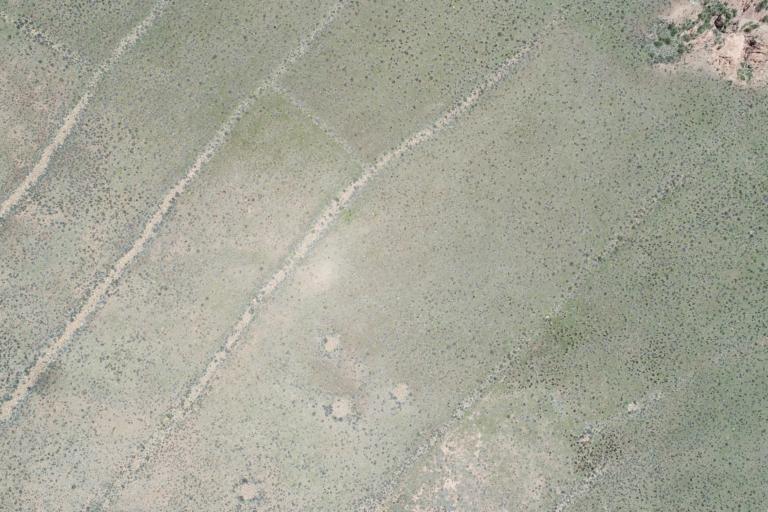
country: BO
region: La Paz
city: Curahuara de Carangas
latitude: -17.3073
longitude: -68.5013
